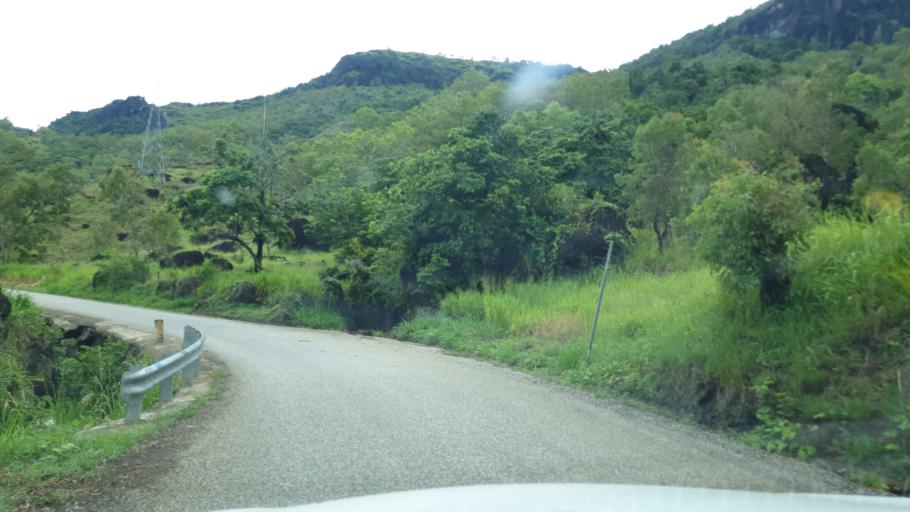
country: PG
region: National Capital
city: Port Moresby
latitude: -9.4193
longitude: 147.3581
